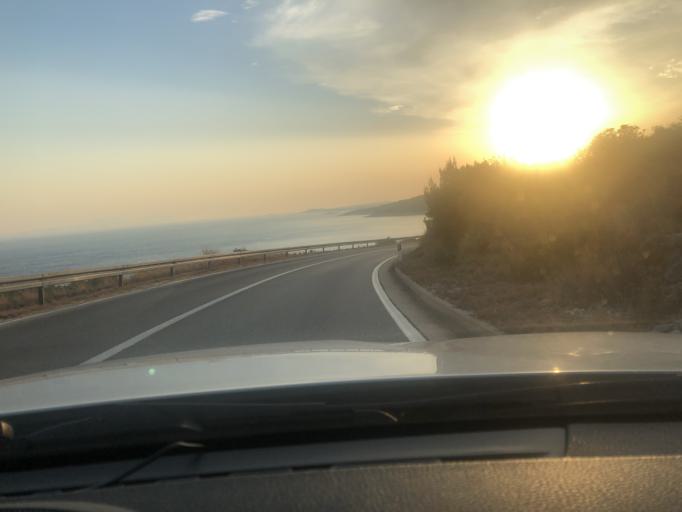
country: HR
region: Splitsko-Dalmatinska
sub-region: Grad Hvar
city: Hvar
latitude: 43.1576
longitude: 16.5043
